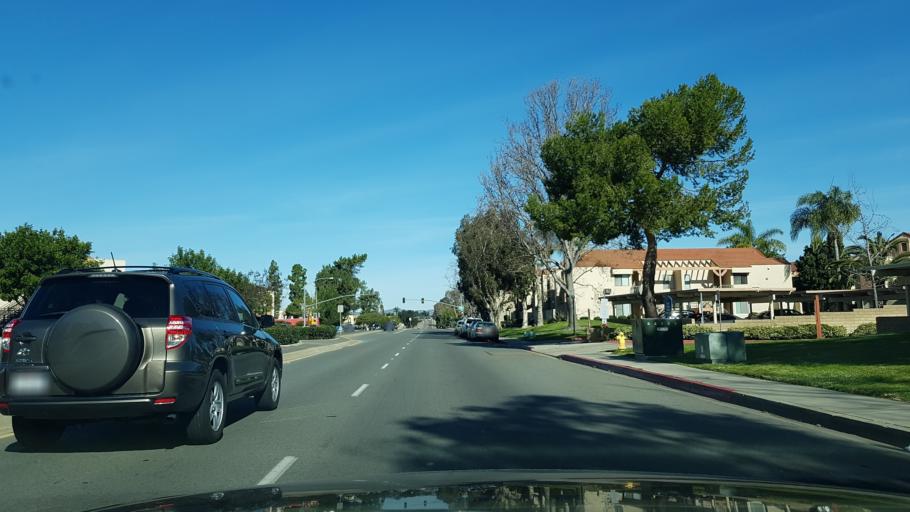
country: US
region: California
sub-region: San Diego County
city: Fairbanks Ranch
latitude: 32.9163
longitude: -117.1439
